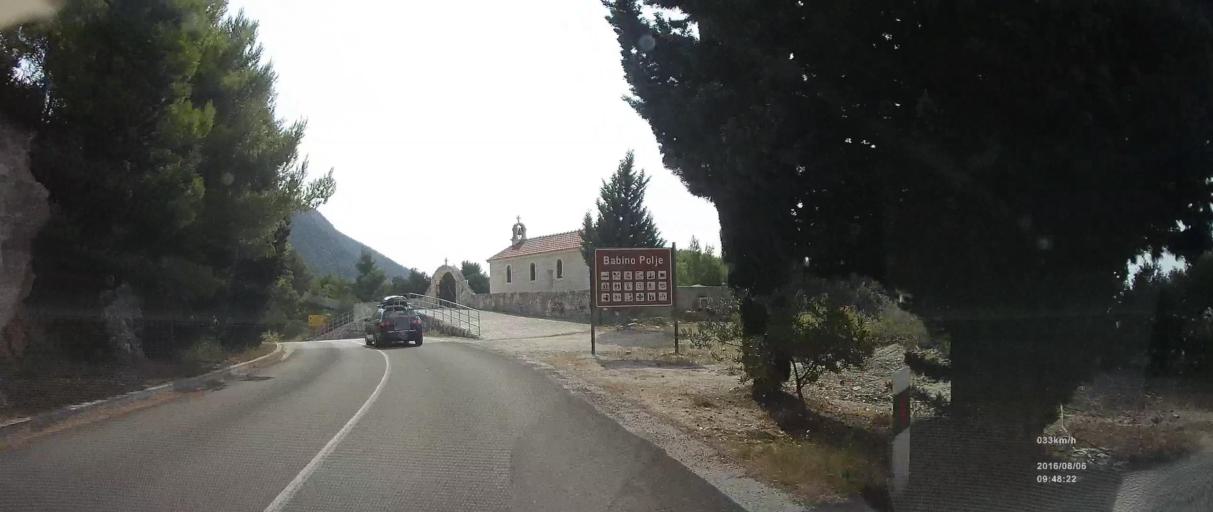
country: HR
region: Dubrovacko-Neretvanska
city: Blato
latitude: 42.7386
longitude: 17.5330
